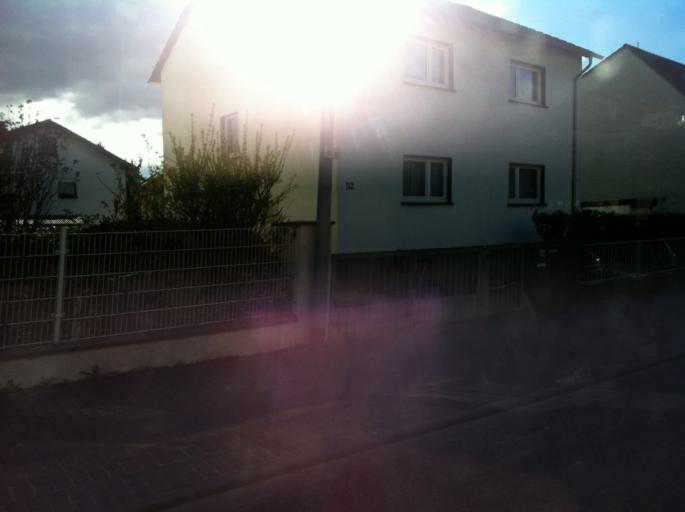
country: DE
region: Hesse
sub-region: Regierungsbezirk Darmstadt
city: Hochheim am Main
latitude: 50.0184
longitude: 8.3541
